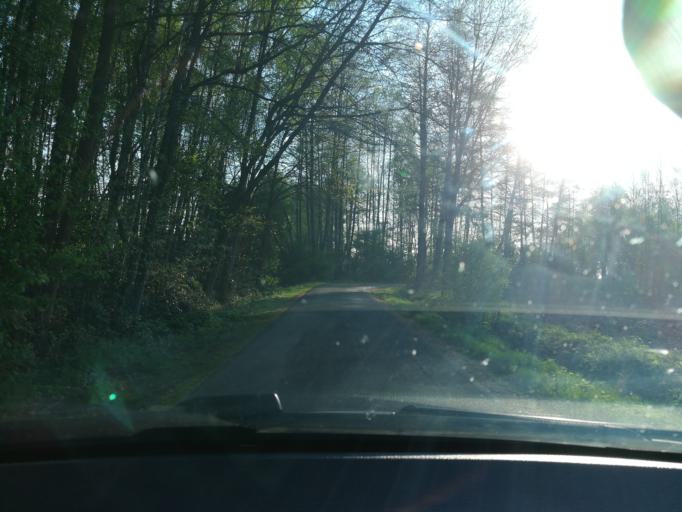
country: DE
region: North Rhine-Westphalia
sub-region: Regierungsbezirk Munster
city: Sassenberg
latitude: 52.0128
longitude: 8.0792
